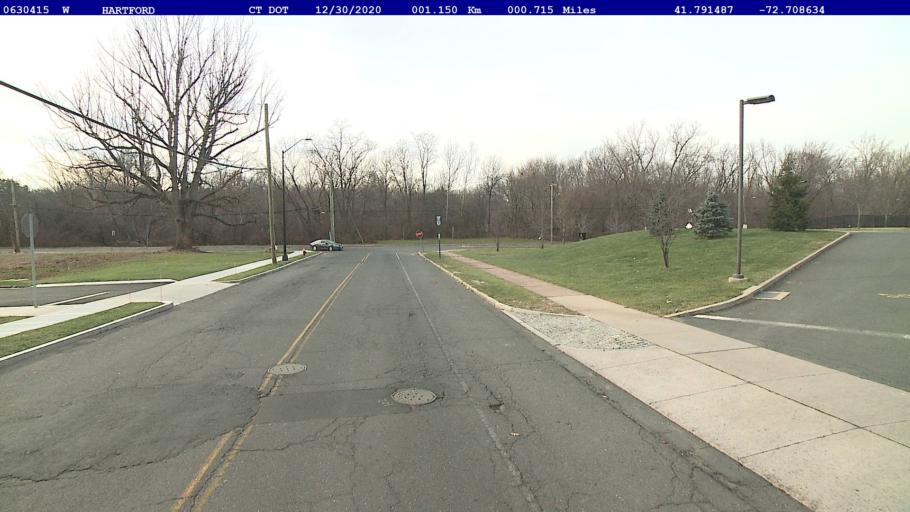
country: US
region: Connecticut
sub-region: Hartford County
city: Blue Hills
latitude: 41.7915
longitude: -72.7086
